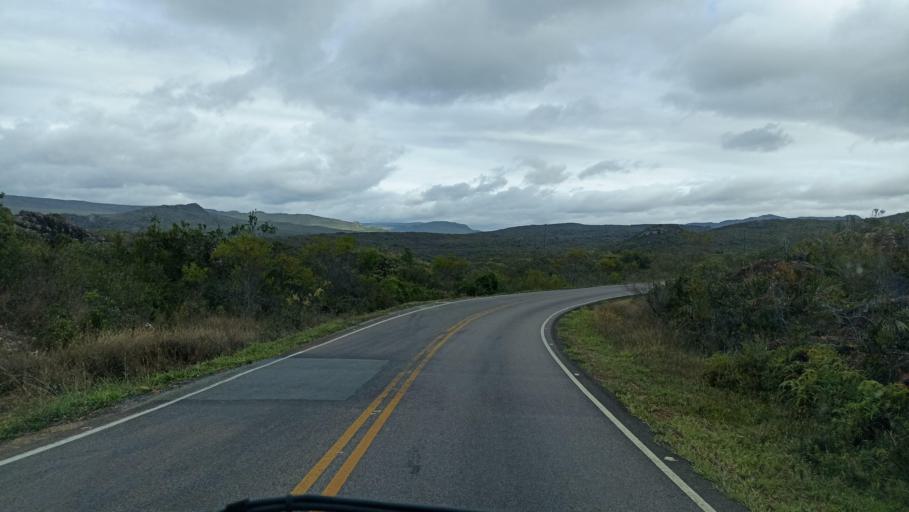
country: BR
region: Bahia
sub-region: Andarai
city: Vera Cruz
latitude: -12.9947
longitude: -41.3578
